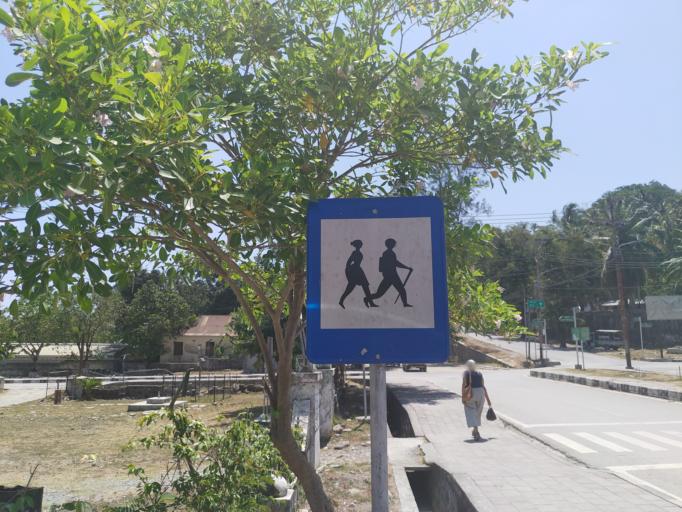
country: TL
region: Viqueque
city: Viqueque
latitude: -8.8671
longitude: 126.3653
